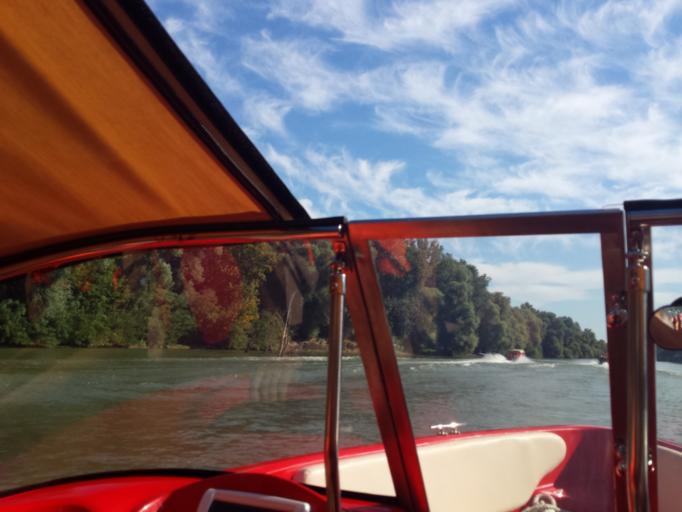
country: RO
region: Tulcea
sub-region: Municipiul Tulcea
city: Tulcea
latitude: 45.2119
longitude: 28.8624
